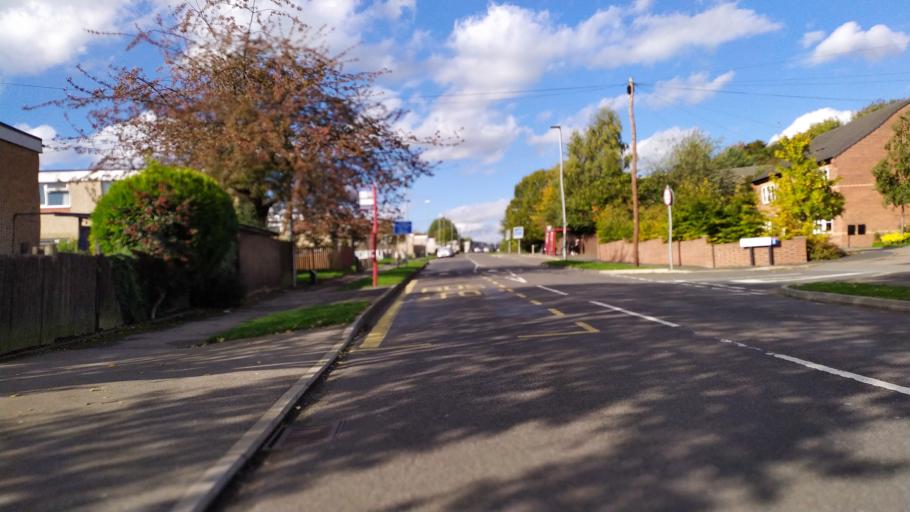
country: GB
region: England
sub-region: City and Borough of Leeds
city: Horsforth
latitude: 53.8221
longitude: -1.5981
